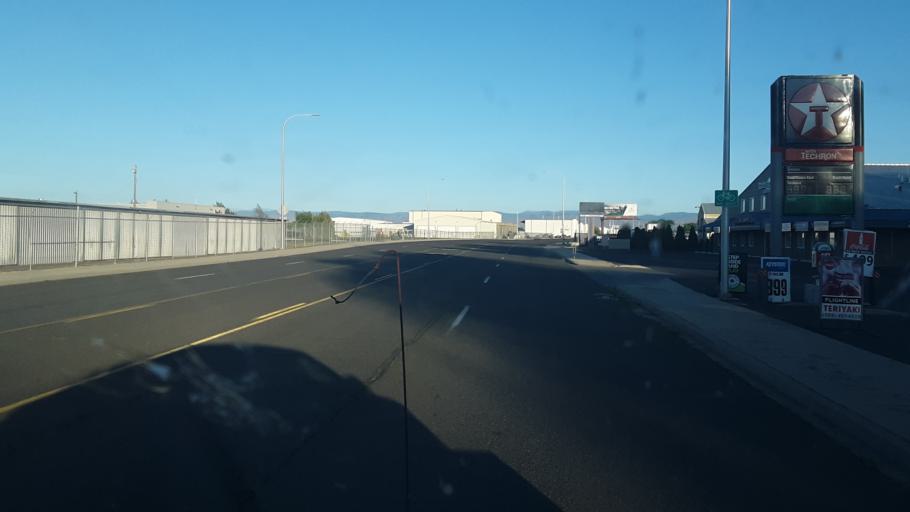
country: US
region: Washington
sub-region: Yakima County
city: Yakima
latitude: 46.5734
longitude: -120.5475
